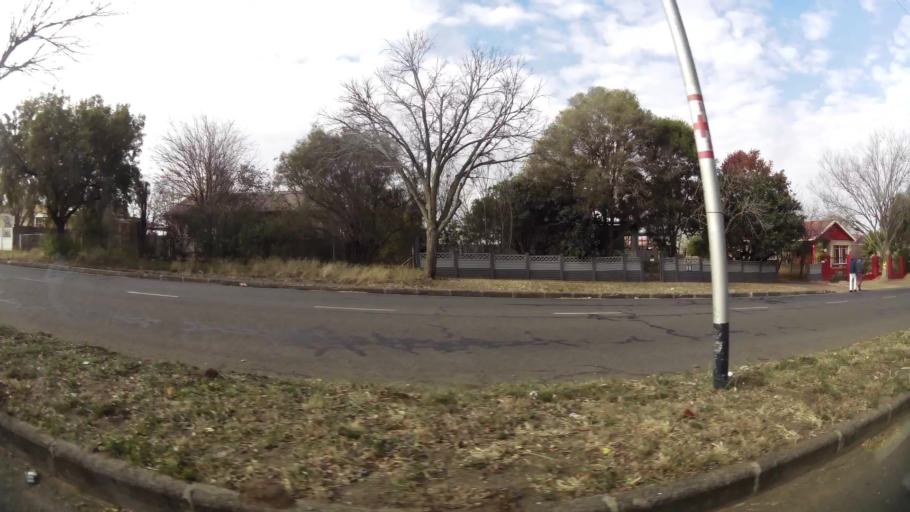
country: ZA
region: Orange Free State
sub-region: Mangaung Metropolitan Municipality
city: Bloemfontein
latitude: -29.0756
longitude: 26.2429
